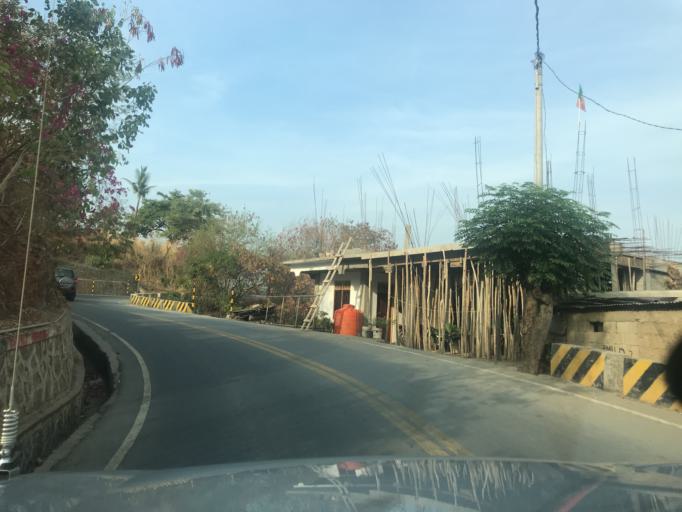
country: TL
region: Dili
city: Dili
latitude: -8.5717
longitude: 125.5885
